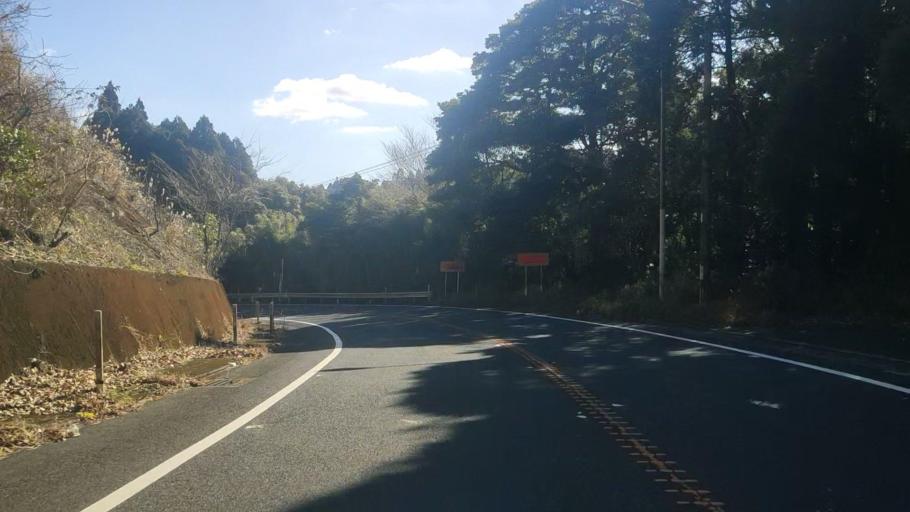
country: JP
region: Kagoshima
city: Sueyoshicho-ninokata
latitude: 31.6622
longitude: 130.8862
